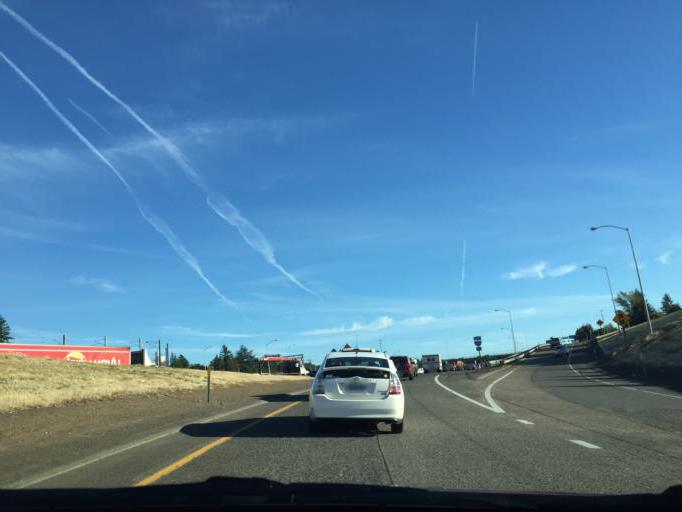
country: US
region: Oregon
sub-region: Multnomah County
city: Lents
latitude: 45.5299
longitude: -122.5658
